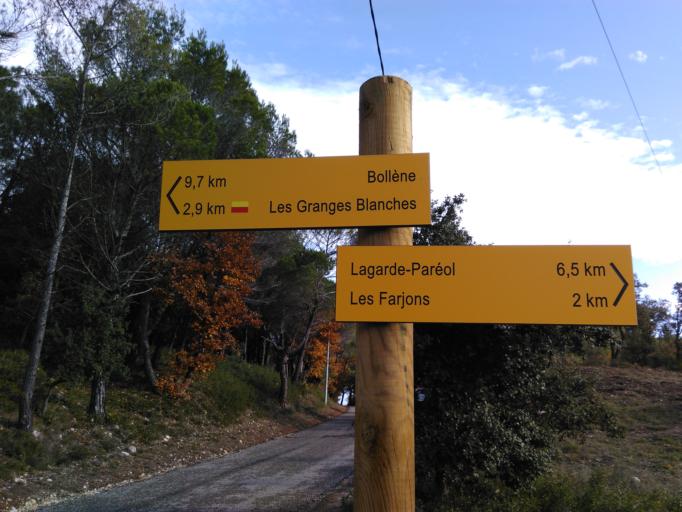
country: FR
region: Rhone-Alpes
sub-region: Departement de la Drome
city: Rochegude
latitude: 44.2470
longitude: 4.8145
